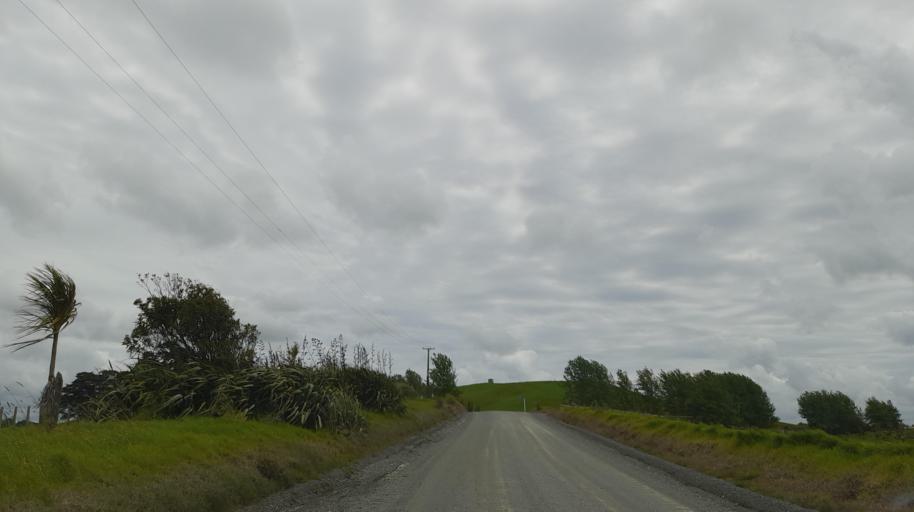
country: NZ
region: Auckland
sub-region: Auckland
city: Wellsford
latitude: -36.2390
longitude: 174.4380
